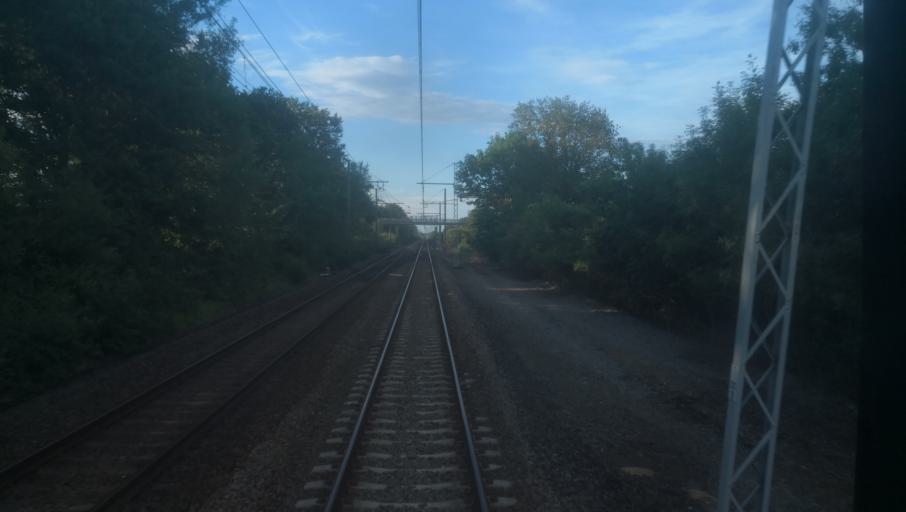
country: FR
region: Centre
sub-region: Departement de l'Indre
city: Luant
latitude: 46.6965
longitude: 1.5642
